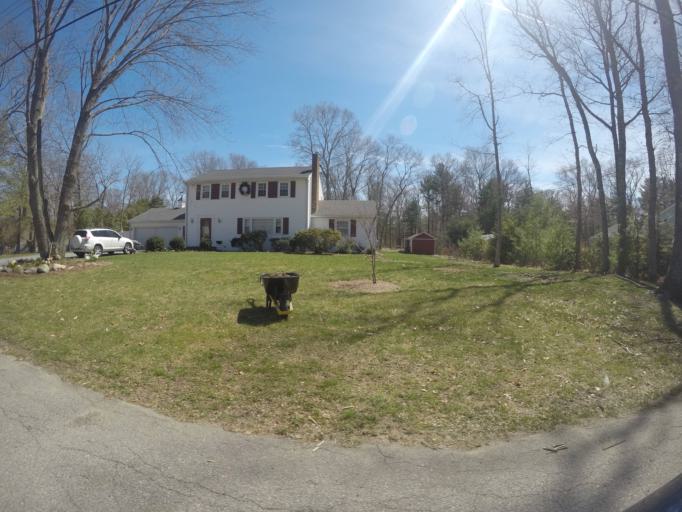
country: US
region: Massachusetts
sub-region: Bristol County
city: Easton
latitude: 42.0372
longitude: -71.0878
